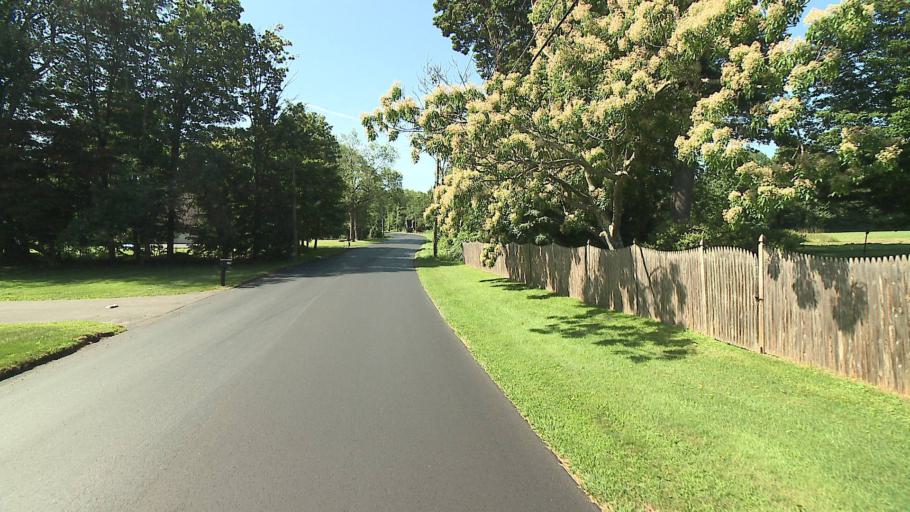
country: US
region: Connecticut
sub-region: Hartford County
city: Tariffville
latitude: 41.9602
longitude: -72.7218
